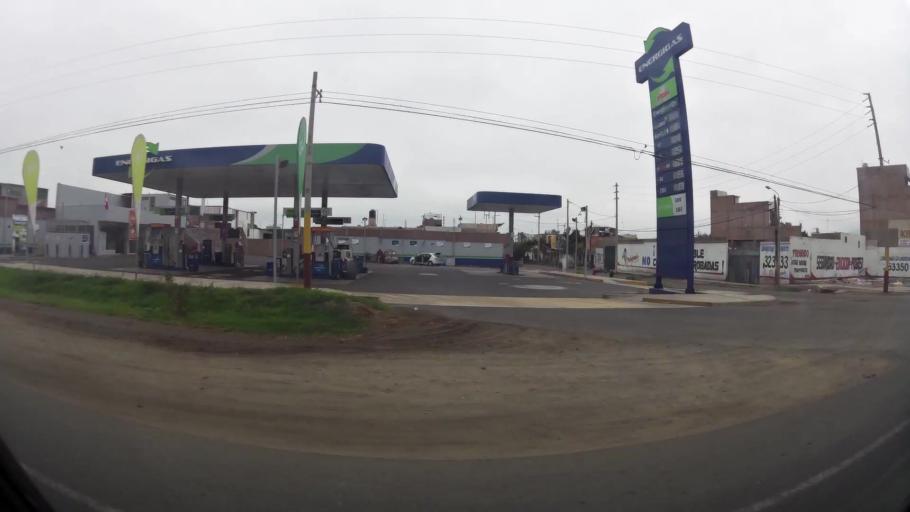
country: PE
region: Ancash
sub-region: Provincia de Santa
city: Chimbote
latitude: -9.0853
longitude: -78.5767
